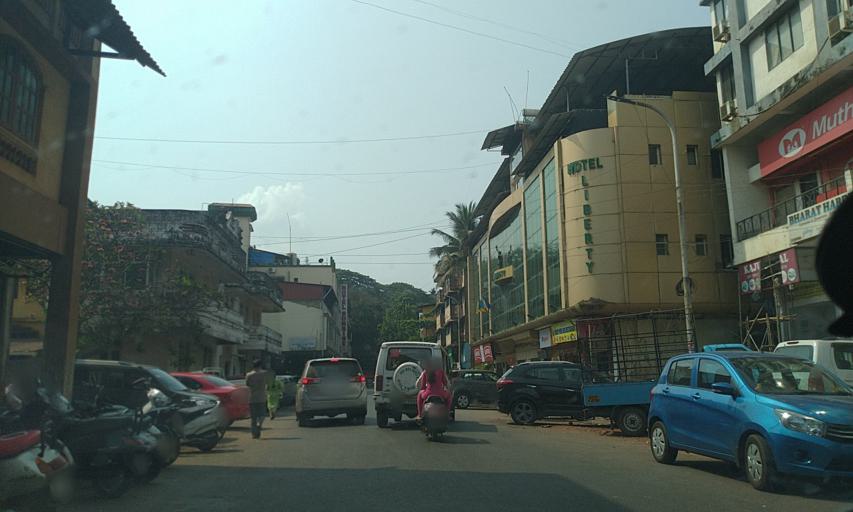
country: IN
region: Goa
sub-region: North Goa
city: Panaji
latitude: 15.4969
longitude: 73.8225
